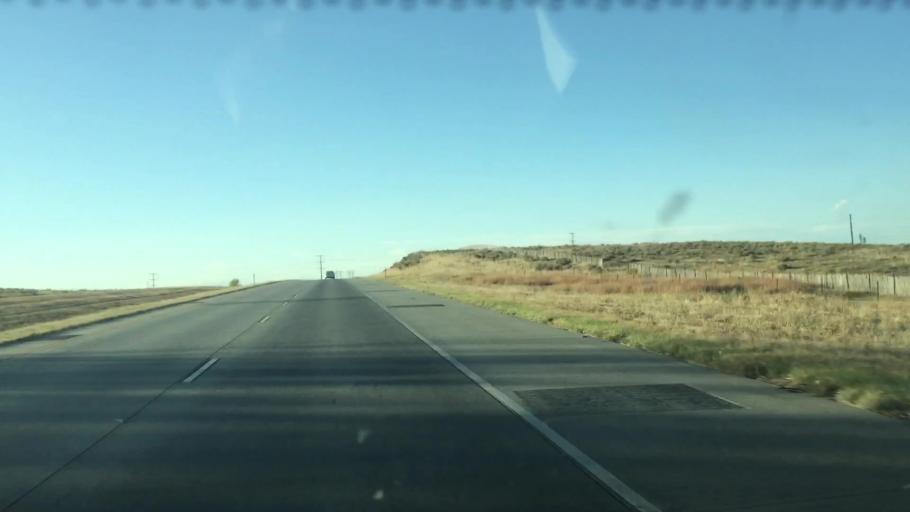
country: US
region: Colorado
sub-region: Arapahoe County
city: Byers
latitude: 39.6594
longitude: -104.0809
